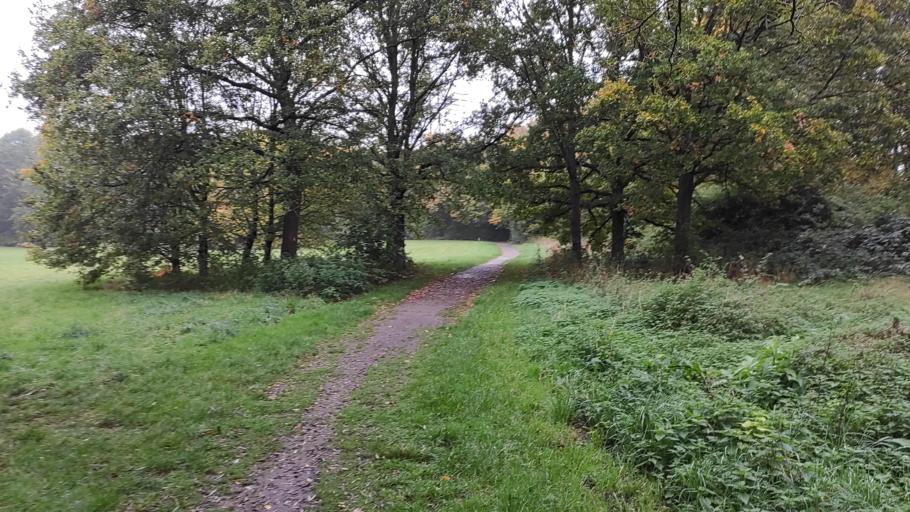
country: DE
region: North Rhine-Westphalia
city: Witten
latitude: 51.4224
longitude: 7.2741
